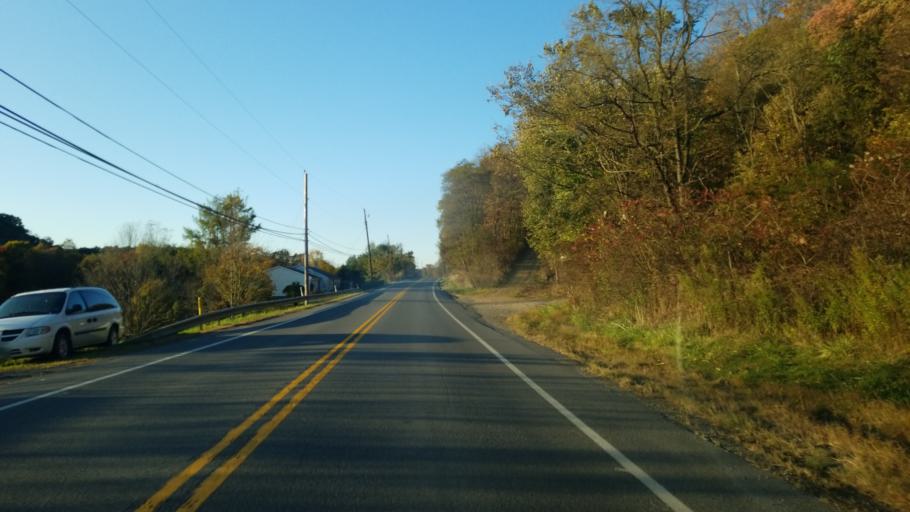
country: US
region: Pennsylvania
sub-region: Jefferson County
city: Punxsutawney
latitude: 40.9592
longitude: -78.9664
